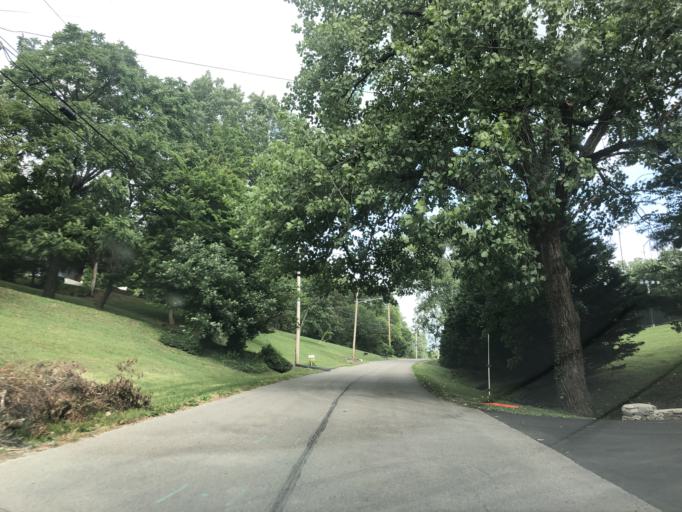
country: US
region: Tennessee
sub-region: Davidson County
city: Oak Hill
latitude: 36.0830
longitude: -86.8146
